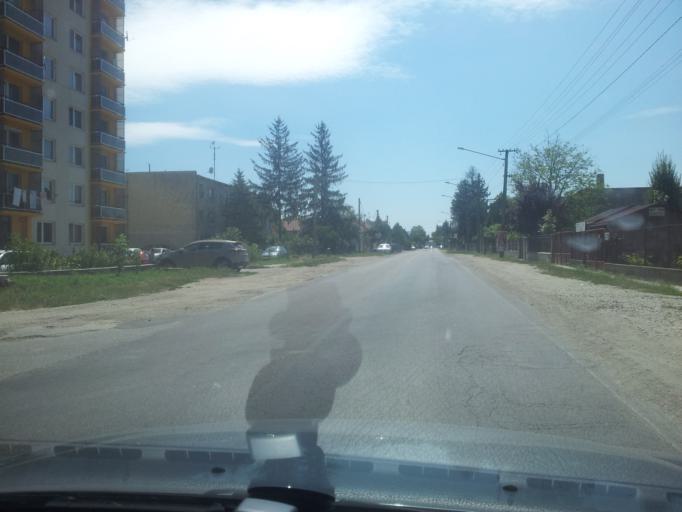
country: SK
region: Nitriansky
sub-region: Okres Nove Zamky
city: Sturovo
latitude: 47.8039
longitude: 18.7102
